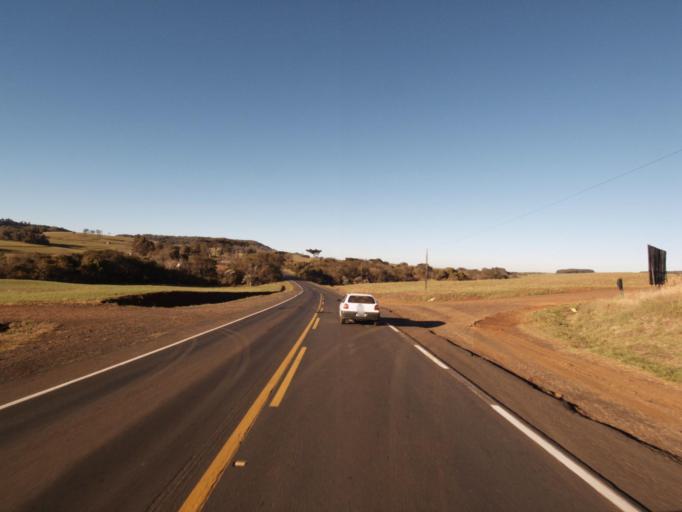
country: AR
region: Misiones
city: Bernardo de Irigoyen
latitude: -26.3413
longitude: -53.5473
